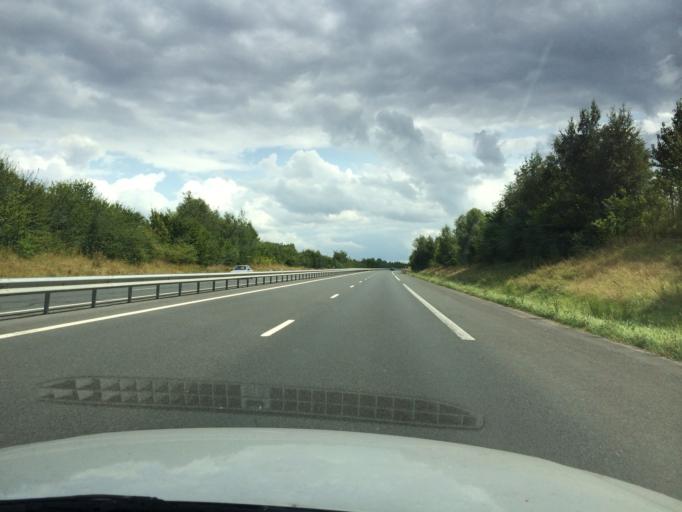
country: FR
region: Lower Normandy
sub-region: Departement du Calvados
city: Port-en-Bessin-Huppain
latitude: 49.3014
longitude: -0.7993
